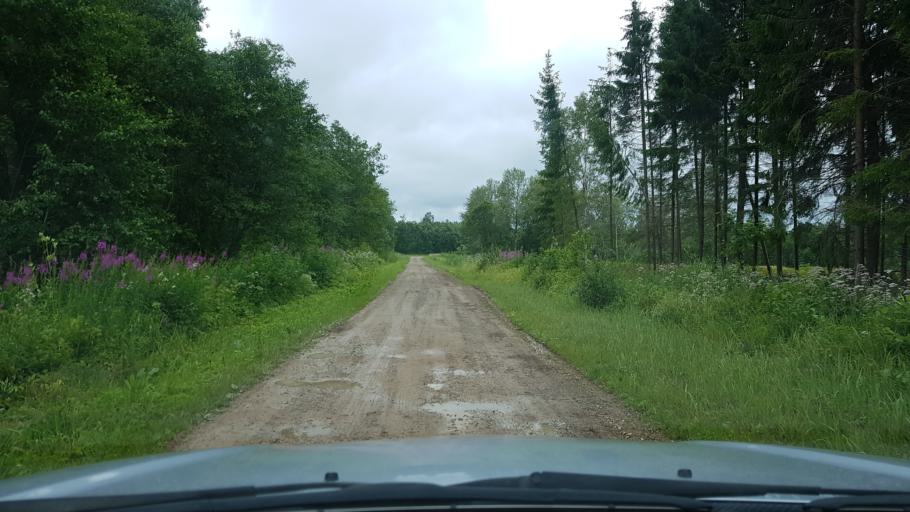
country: EE
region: Ida-Virumaa
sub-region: Narva-Joesuu linn
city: Narva-Joesuu
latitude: 59.3653
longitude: 27.9233
